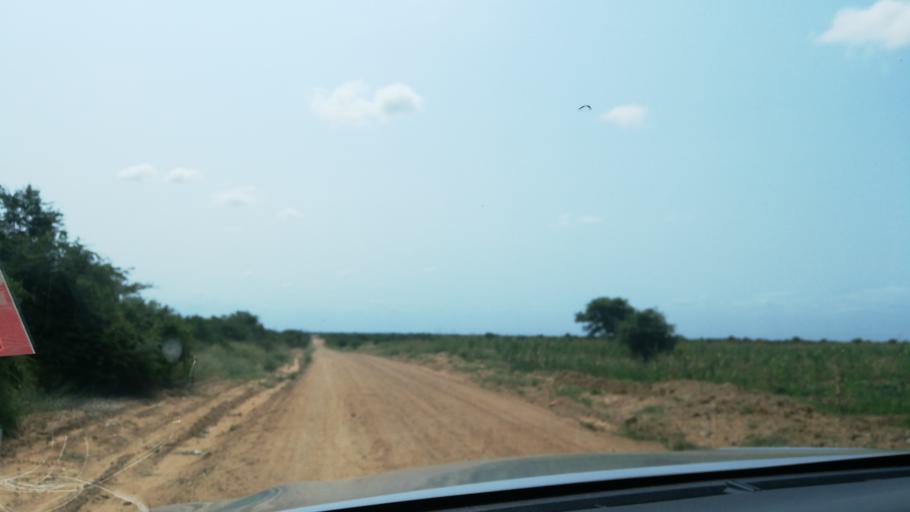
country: MZ
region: Maputo
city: Matola
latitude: -26.0829
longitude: 32.3914
